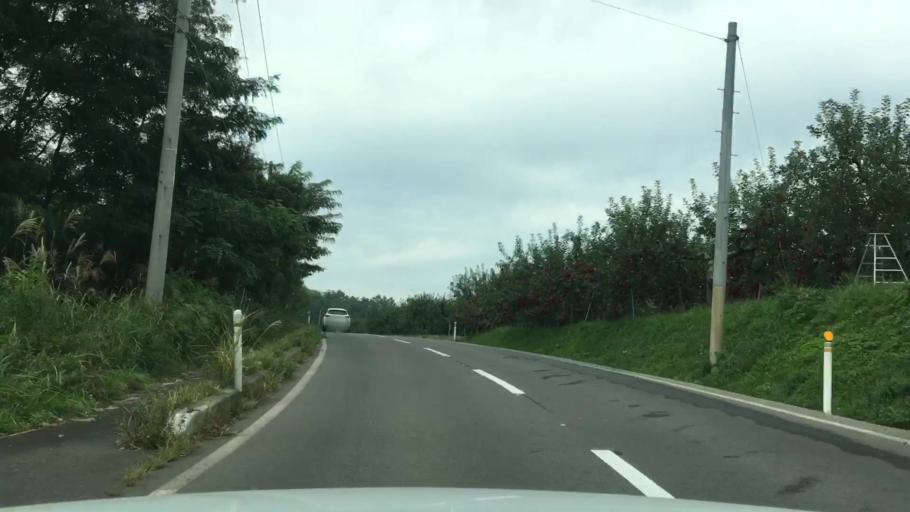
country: JP
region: Aomori
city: Hirosaki
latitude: 40.6680
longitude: 140.3942
